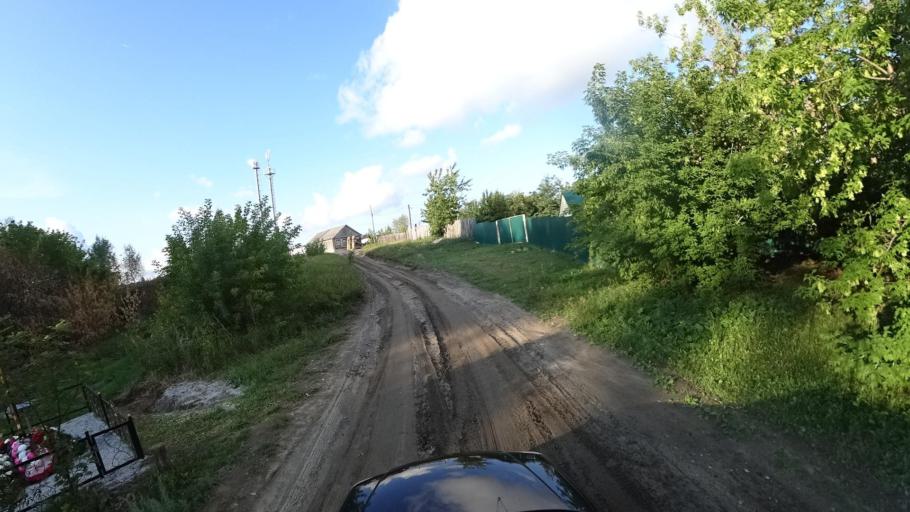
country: RU
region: Sverdlovsk
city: Kamyshlov
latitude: 56.8487
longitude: 62.6627
